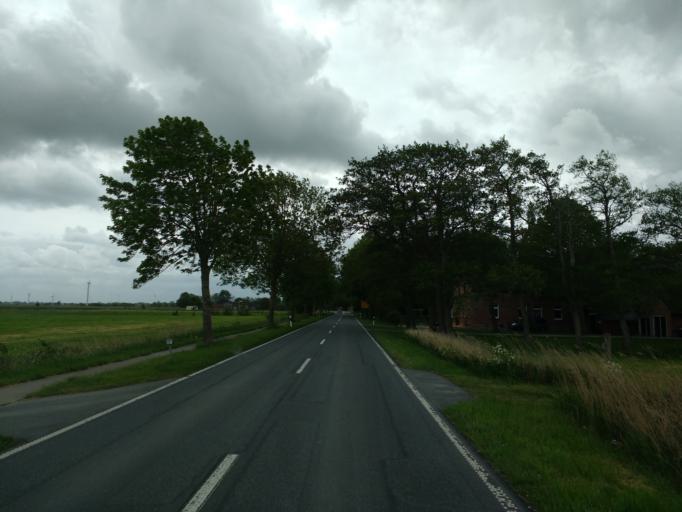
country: DE
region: Lower Saxony
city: Schillig
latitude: 53.6691
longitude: 7.9864
